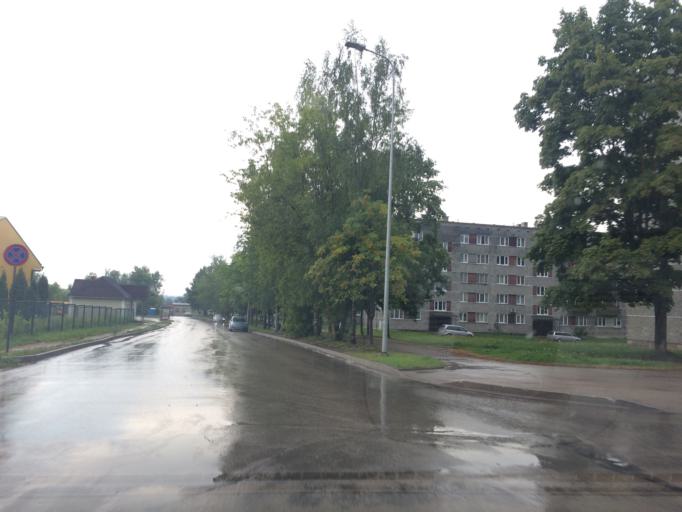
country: LV
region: Rezekne
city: Rezekne
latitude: 56.5233
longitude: 27.3522
